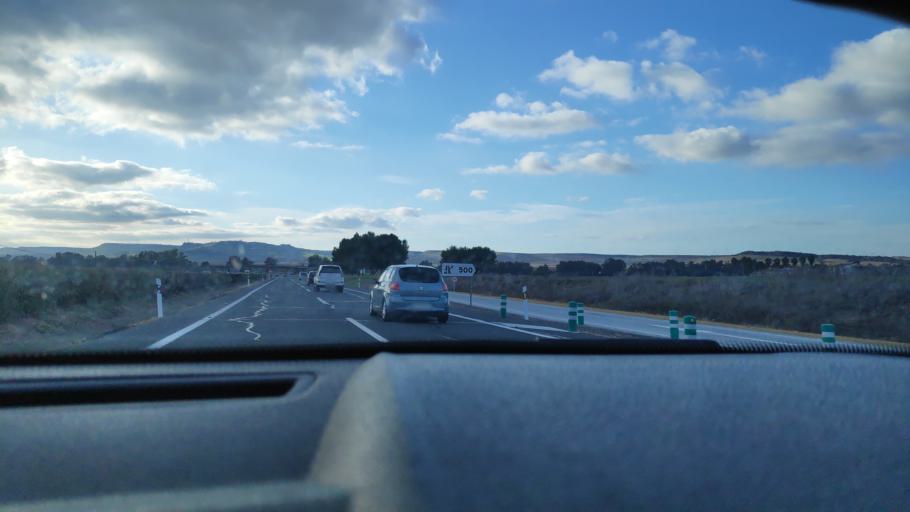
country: ES
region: Andalusia
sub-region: Provincia de Sevilla
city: Carmona
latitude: 37.4814
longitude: -5.5659
